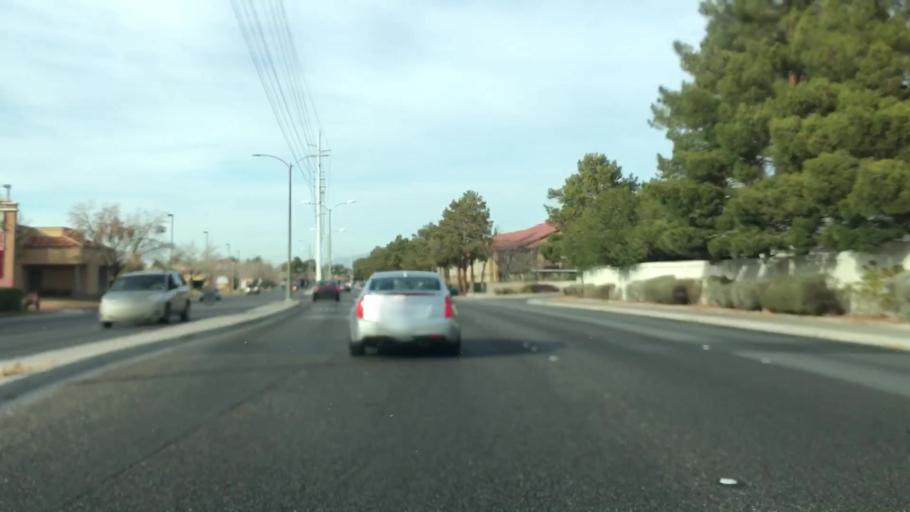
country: US
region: Nevada
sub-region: Clark County
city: Whitney
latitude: 36.0534
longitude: -115.0826
